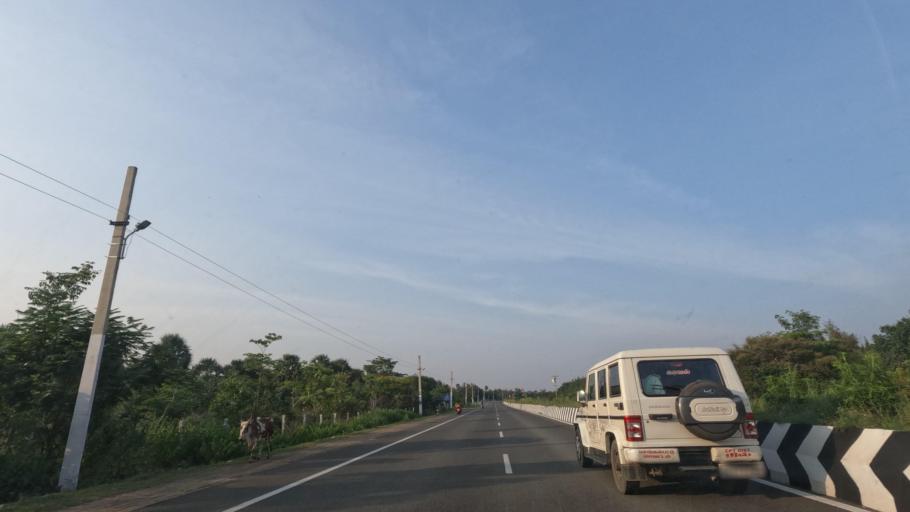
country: IN
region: Tamil Nadu
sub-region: Kancheepuram
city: Mamallapuram
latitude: 12.6649
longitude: 80.2095
